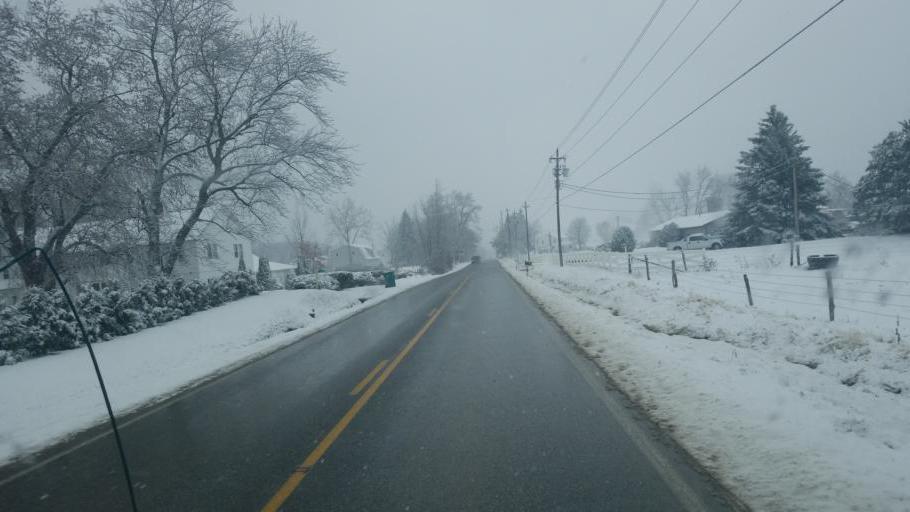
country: US
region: Ohio
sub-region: Geauga County
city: Middlefield
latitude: 41.4129
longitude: -81.0982
